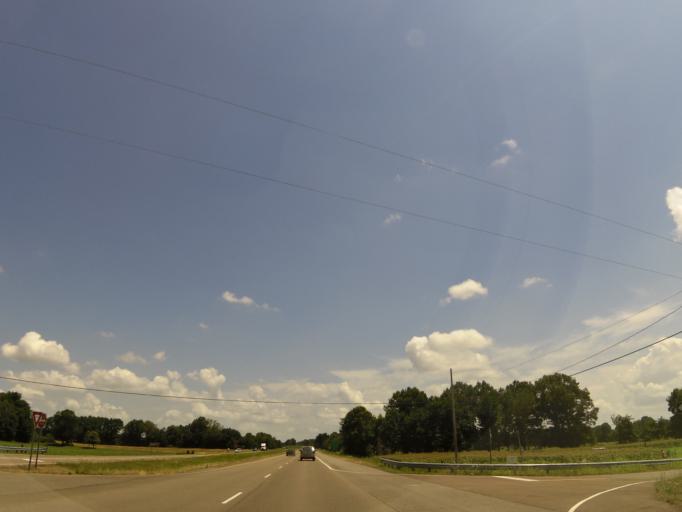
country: US
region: Tennessee
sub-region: Crockett County
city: Alamo
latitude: 35.8453
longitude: -89.1925
